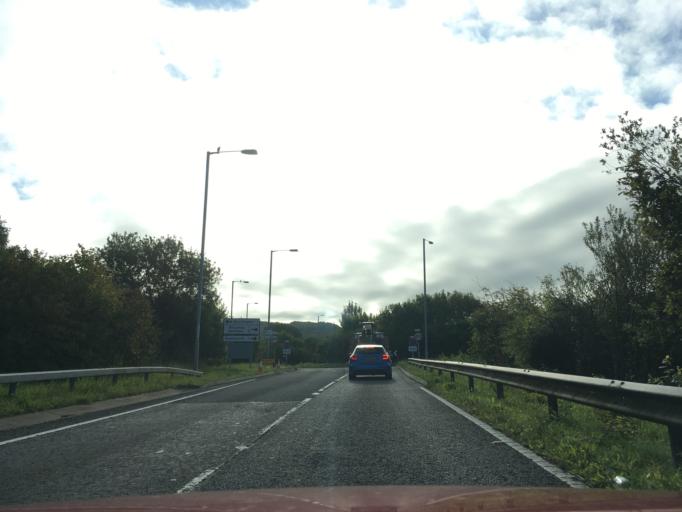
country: GB
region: England
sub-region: Gloucestershire
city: Shurdington
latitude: 51.8503
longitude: -2.1401
